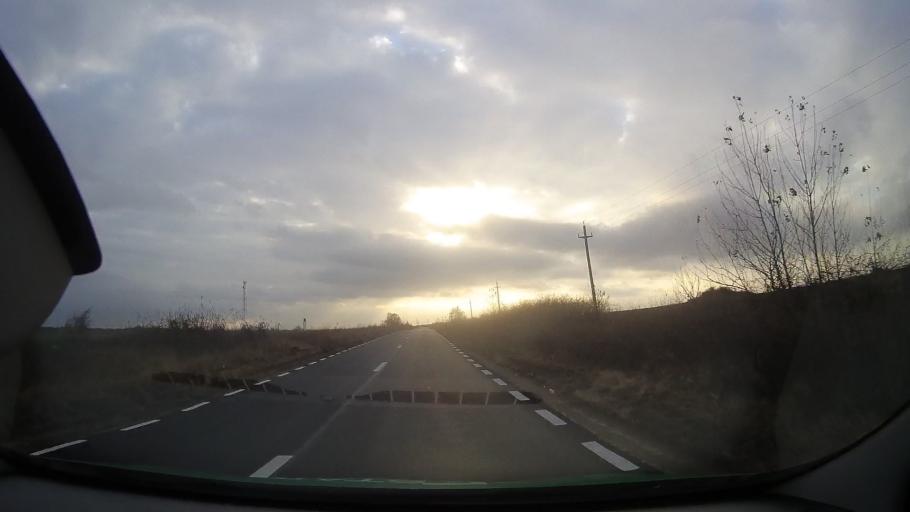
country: RO
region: Constanta
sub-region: Comuna Adamclisi
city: Adamclisi
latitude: 44.0704
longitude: 27.9810
